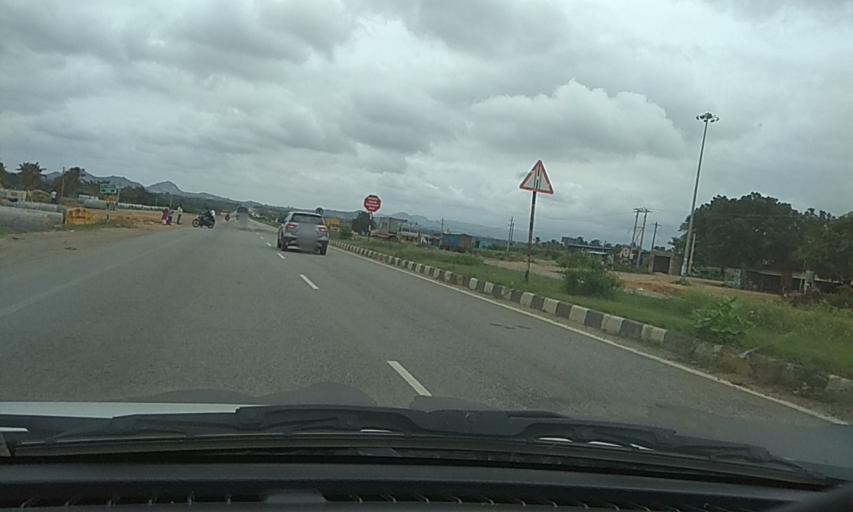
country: IN
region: Karnataka
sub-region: Chitradurga
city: Chitradurga
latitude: 14.2806
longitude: 76.3078
